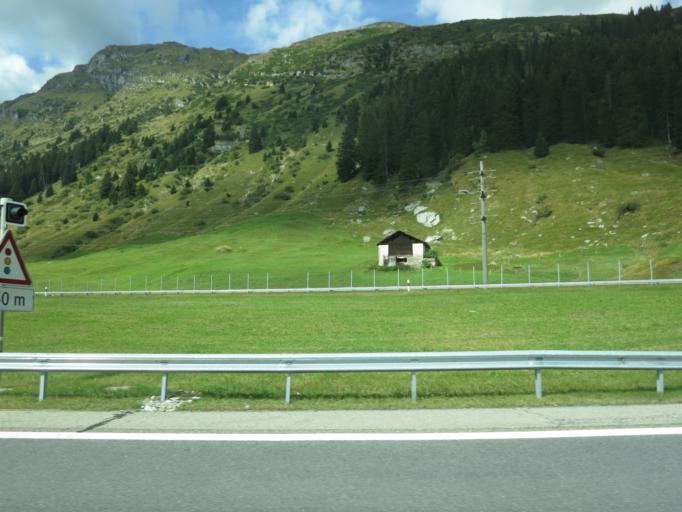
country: CH
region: Grisons
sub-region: Hinterrhein District
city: Hinterrhein
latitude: 46.5280
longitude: 9.1899
